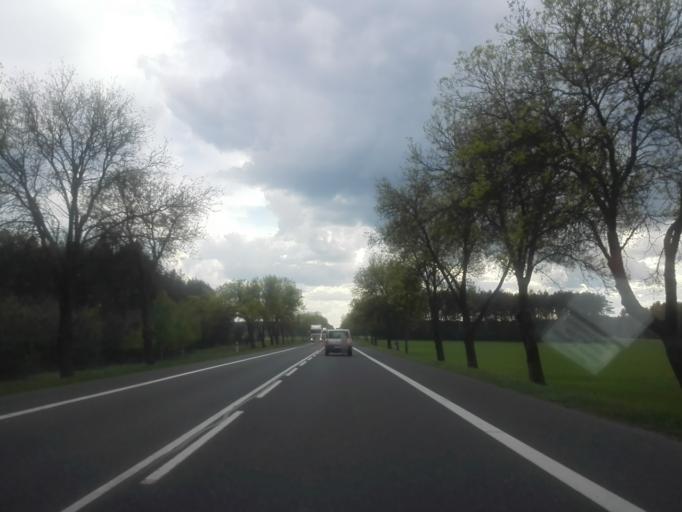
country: PL
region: Podlasie
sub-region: Powiat zambrowski
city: Szumowo
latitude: 52.8582
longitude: 21.9970
